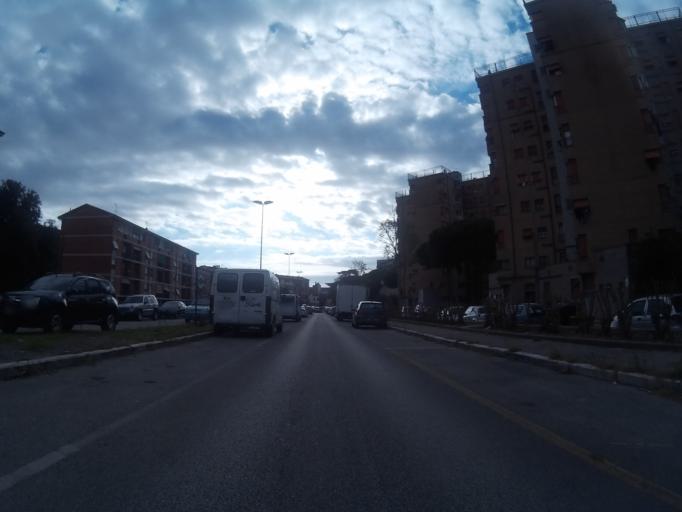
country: IT
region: Tuscany
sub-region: Provincia di Livorno
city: Livorno
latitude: 43.5589
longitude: 10.3210
